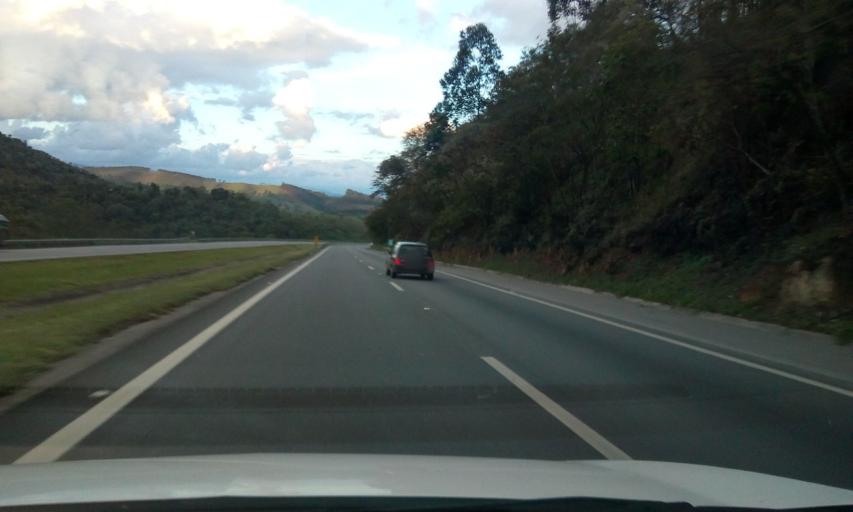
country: BR
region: Sao Paulo
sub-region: Santa Isabel
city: Santa Isabel
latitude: -23.1685
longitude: -46.2403
